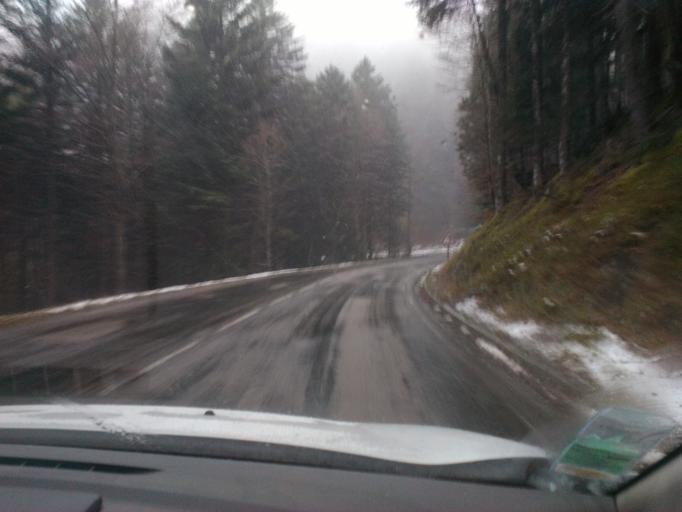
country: FR
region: Lorraine
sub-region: Departement des Vosges
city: Xonrupt-Longemer
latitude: 48.0644
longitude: 6.9806
